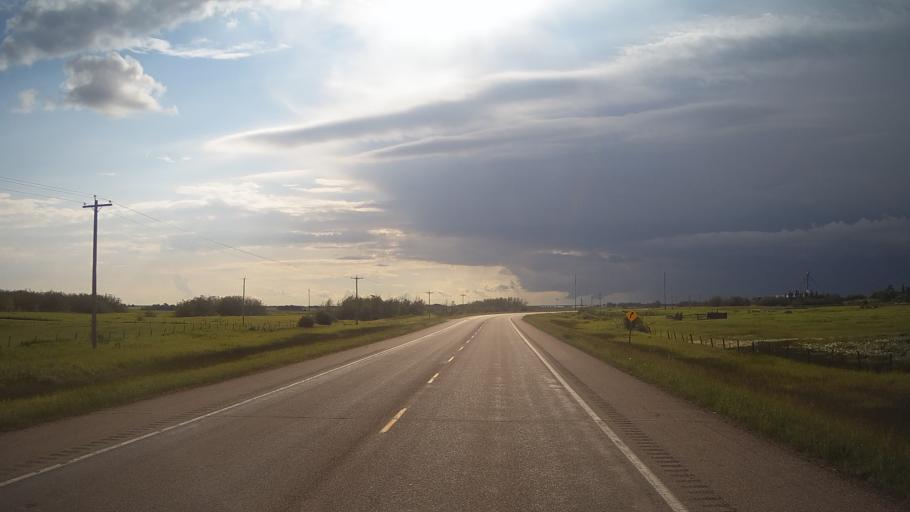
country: CA
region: Alberta
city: Vegreville
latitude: 53.2216
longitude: -112.2135
